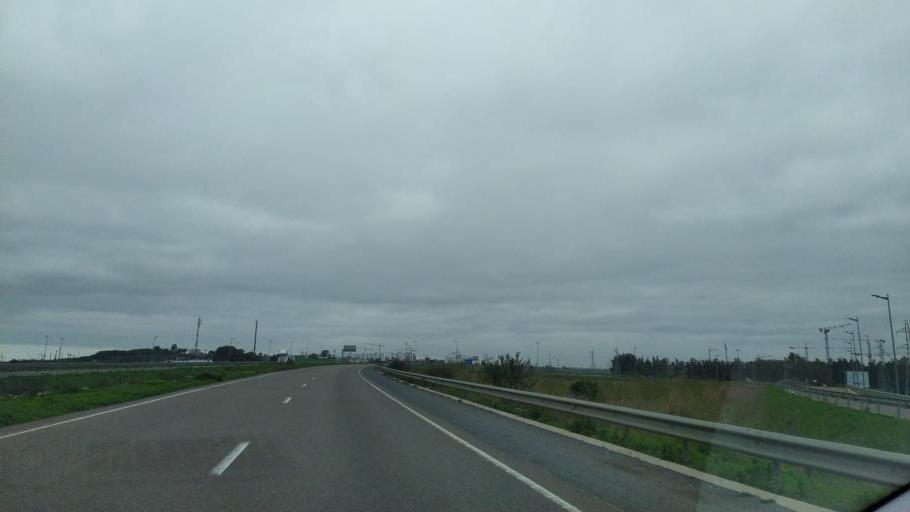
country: MA
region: Rabat-Sale-Zemmour-Zaer
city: Sale
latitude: 33.9737
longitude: -6.7375
